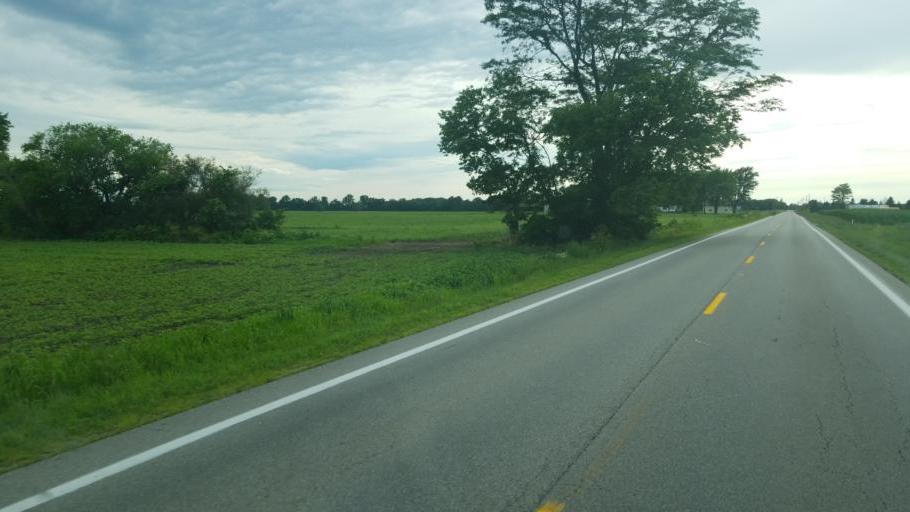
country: US
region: Ohio
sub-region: Delaware County
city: Ashley
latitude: 40.4097
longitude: -82.9674
